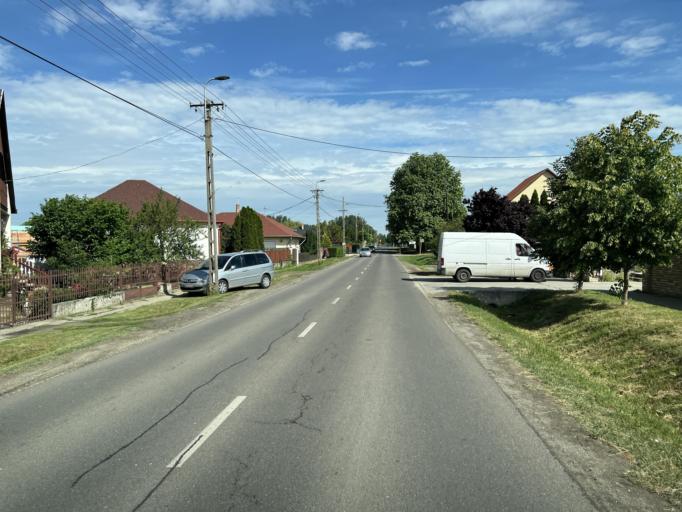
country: HU
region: Pest
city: Isaszeg
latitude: 47.5460
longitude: 19.3891
